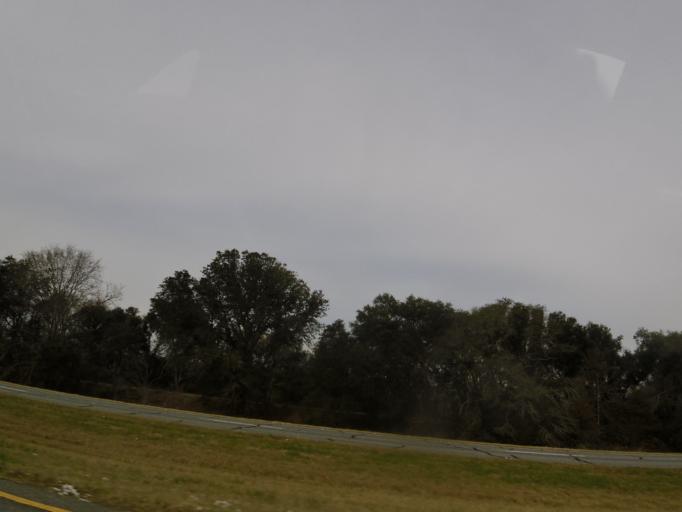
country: US
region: Georgia
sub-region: Seminole County
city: Donalsonville
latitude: 31.0050
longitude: -84.7939
